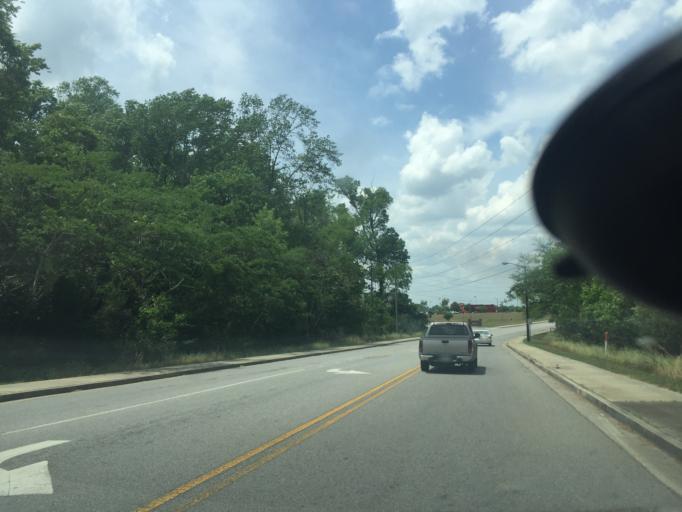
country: US
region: Georgia
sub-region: Bulloch County
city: Statesboro
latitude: 32.4278
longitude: -81.7523
